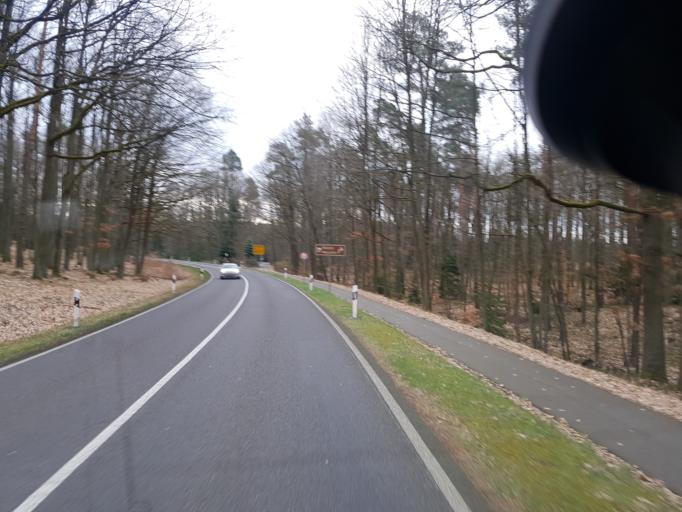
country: DE
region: Brandenburg
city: Gross Lindow
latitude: 52.1729
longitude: 14.4870
